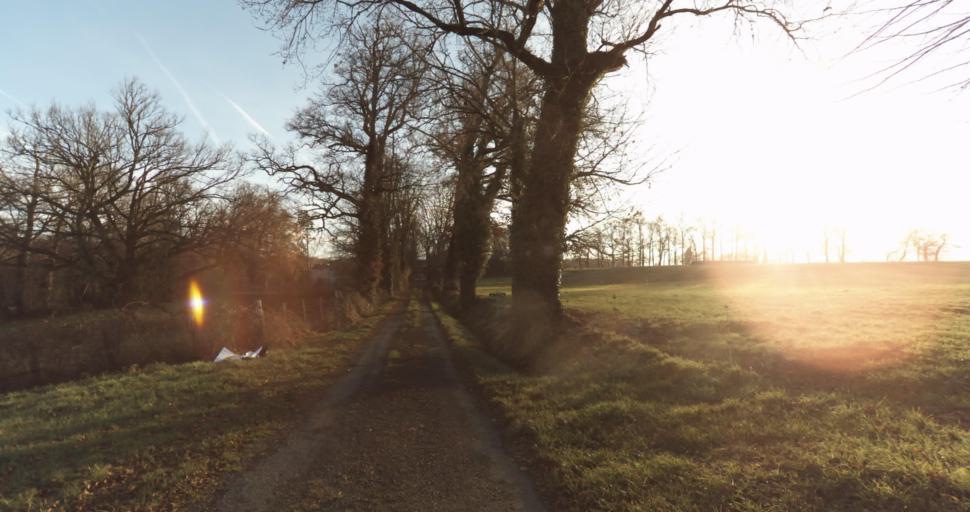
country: FR
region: Limousin
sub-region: Departement de la Haute-Vienne
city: Aixe-sur-Vienne
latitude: 45.7804
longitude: 1.1458
